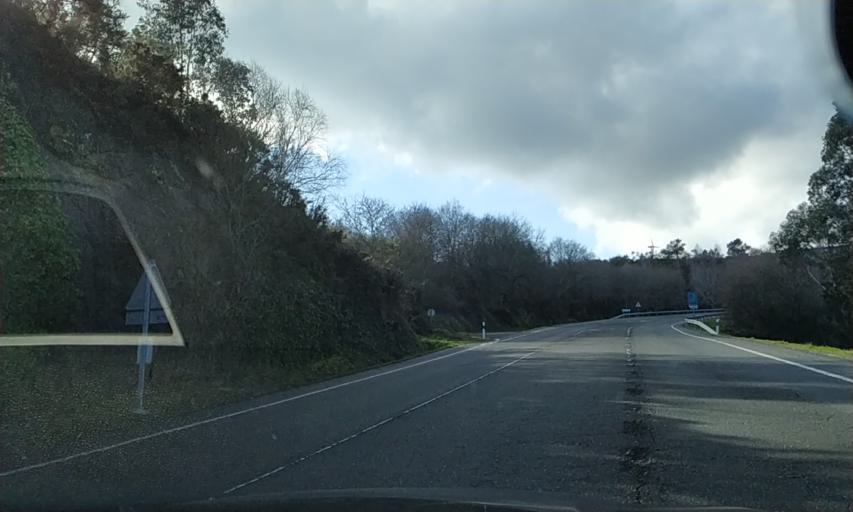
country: ES
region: Galicia
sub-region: Provincia de Pontevedra
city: Silleda
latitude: 42.6978
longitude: -8.3296
